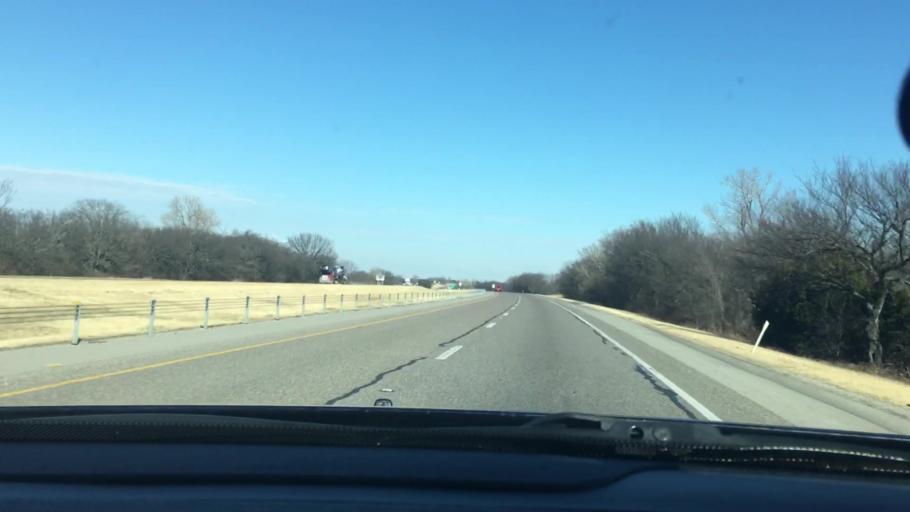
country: US
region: Oklahoma
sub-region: Murray County
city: Davis
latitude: 34.3845
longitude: -97.1419
